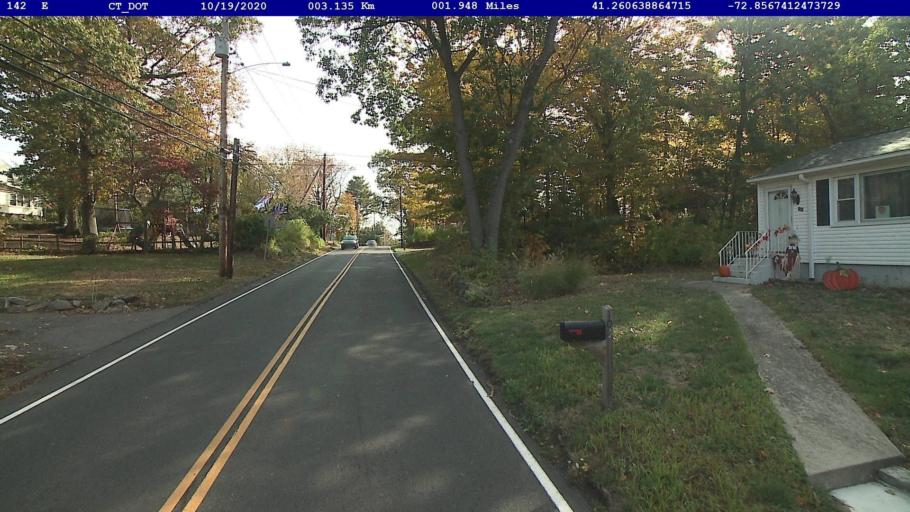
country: US
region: Connecticut
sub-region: New Haven County
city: East Haven
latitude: 41.2605
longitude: -72.8567
